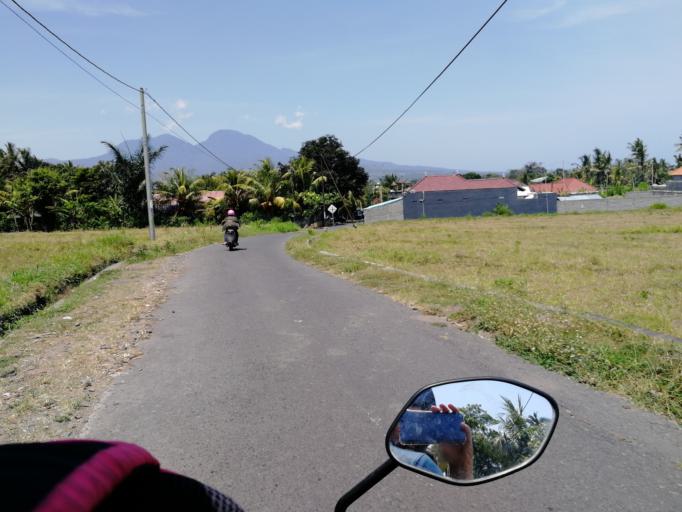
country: ID
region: Bali
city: Banjar Timbrah
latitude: -8.4669
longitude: 115.5922
